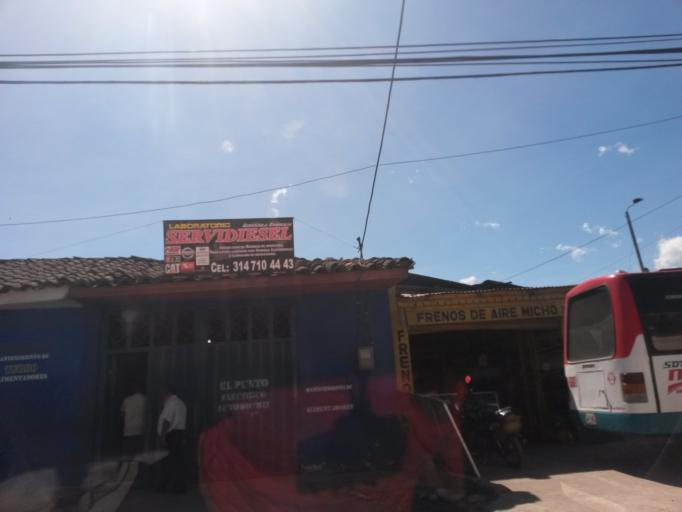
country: CO
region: Cauca
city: Popayan
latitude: 2.4511
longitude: -76.6282
